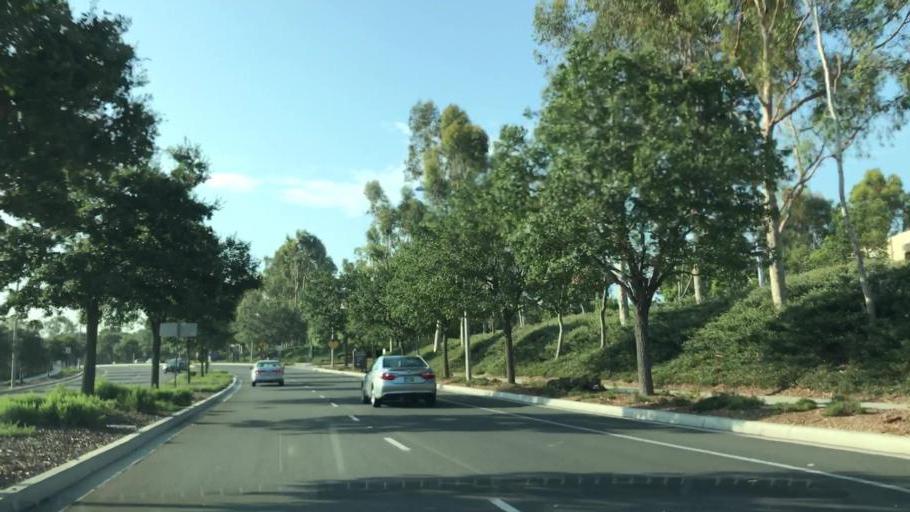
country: US
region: California
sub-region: Orange County
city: San Joaquin Hills
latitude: 33.6425
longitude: -117.8547
